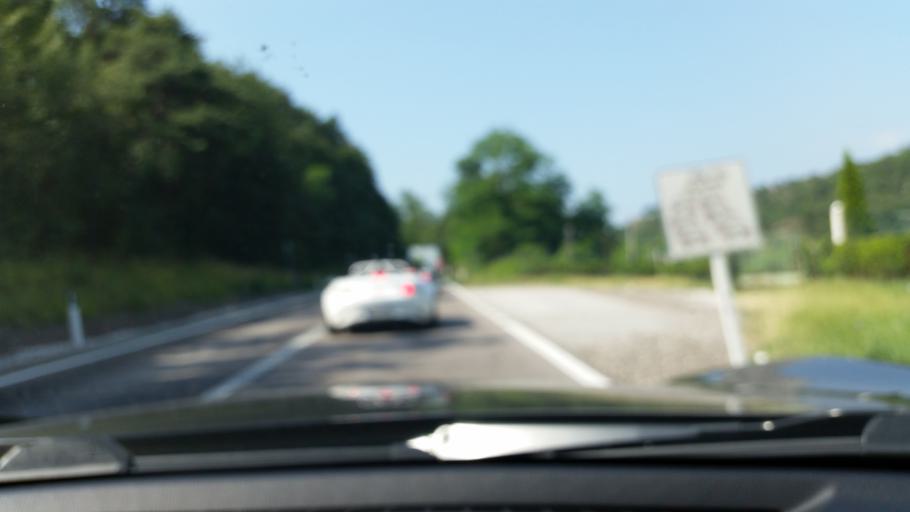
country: IT
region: Trentino-Alto Adige
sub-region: Bolzano
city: Ora
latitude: 46.3403
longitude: 11.2976
